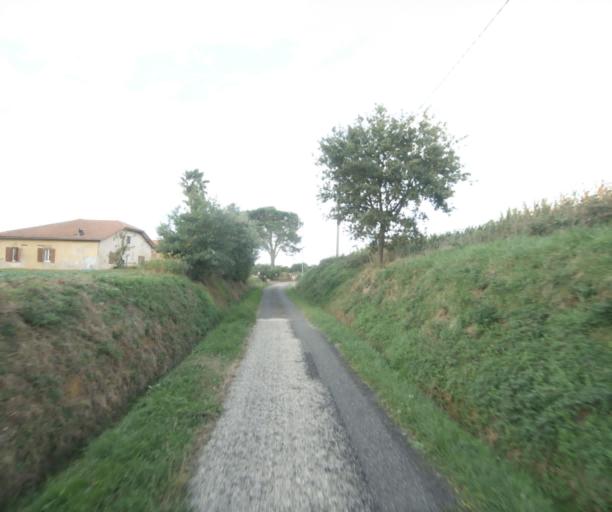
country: FR
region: Midi-Pyrenees
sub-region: Departement du Gers
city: Le Houga
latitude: 43.8431
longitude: -0.1372
